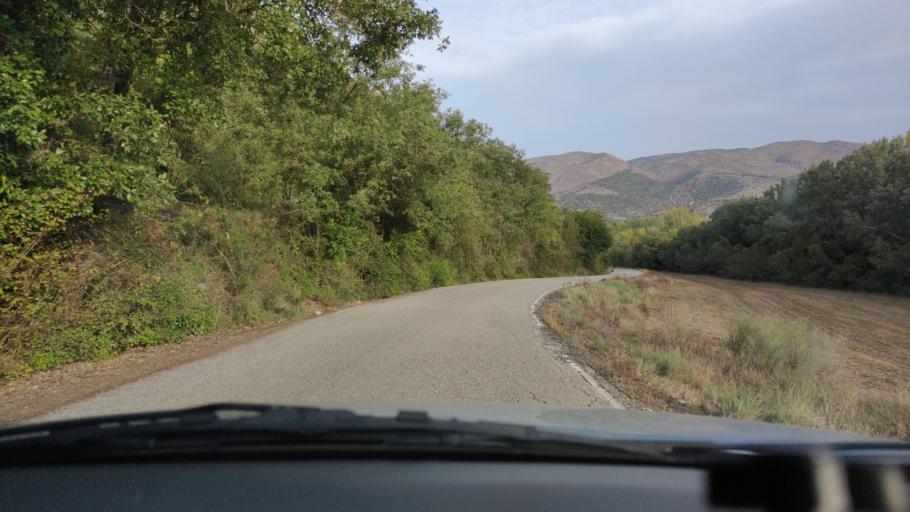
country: ES
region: Catalonia
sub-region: Provincia de Lleida
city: Cubells
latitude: 41.9055
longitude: 0.9704
